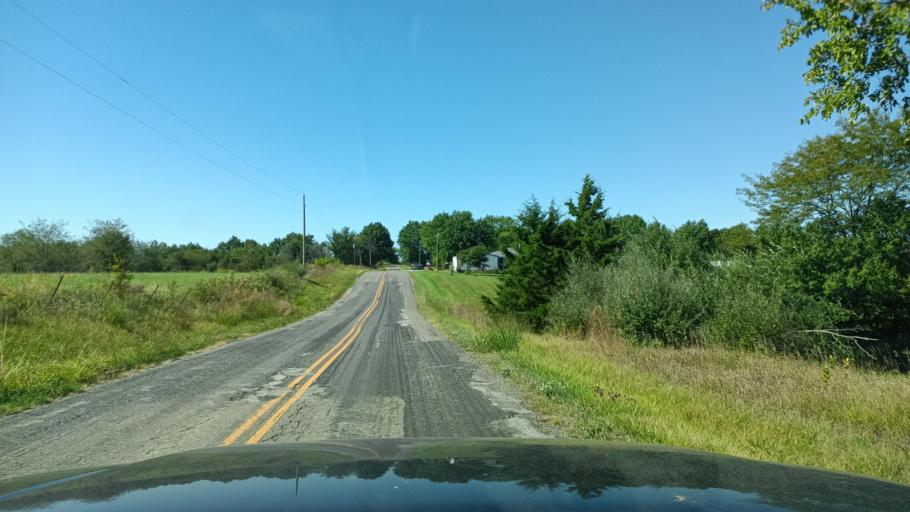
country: US
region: Missouri
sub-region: Scotland County
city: Memphis
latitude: 40.3555
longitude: -92.2618
